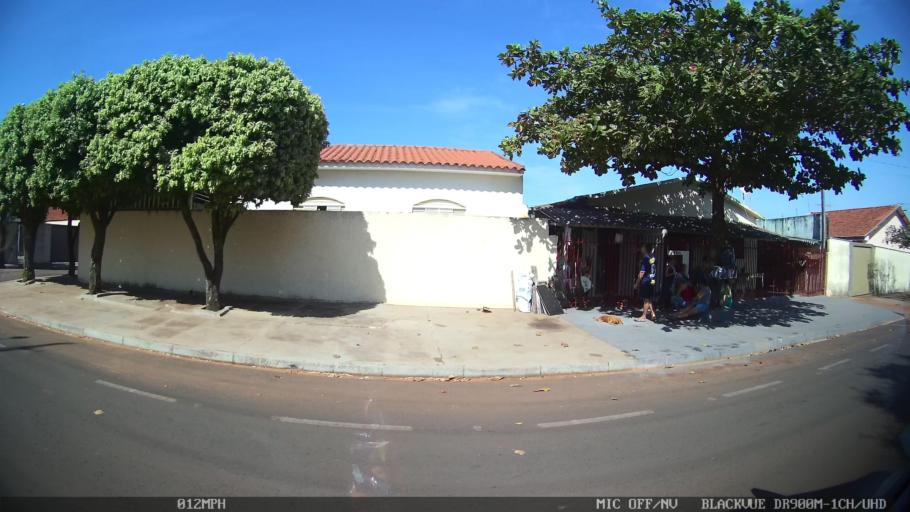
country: BR
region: Sao Paulo
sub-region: Sao Jose Do Rio Preto
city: Sao Jose do Rio Preto
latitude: -20.7861
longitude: -49.4011
